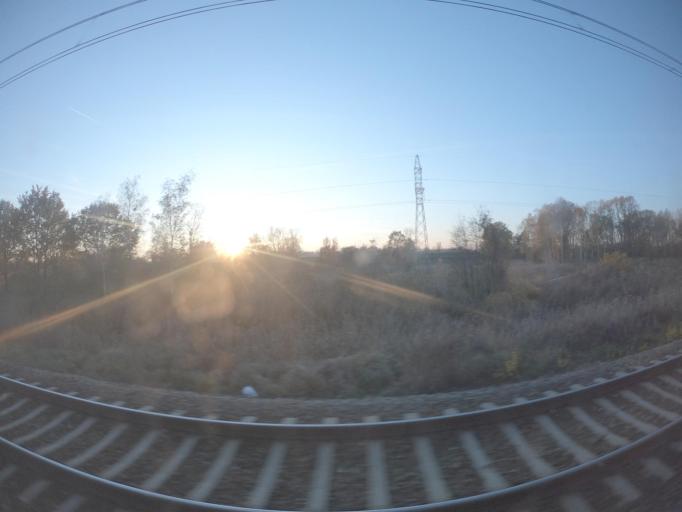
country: PL
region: Lubusz
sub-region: Powiat gorzowski
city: Kostrzyn nad Odra
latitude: 52.5704
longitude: 14.6449
